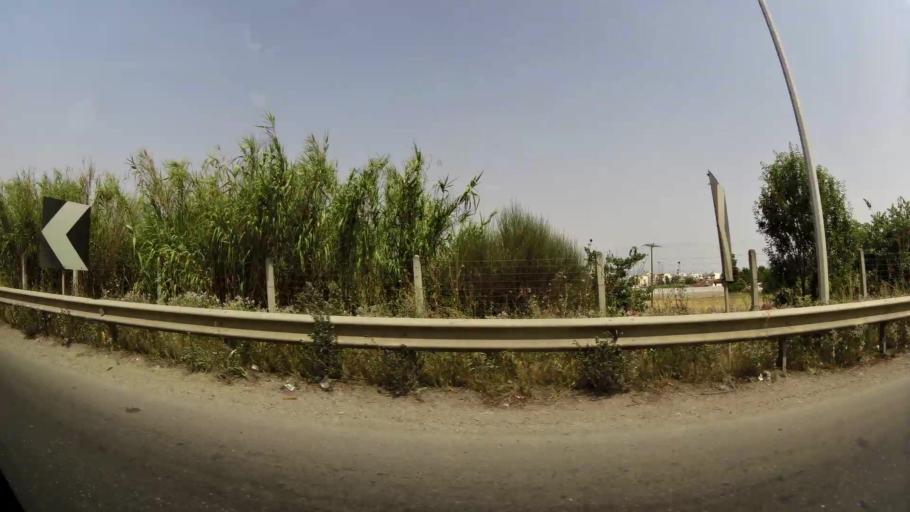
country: GR
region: Central Macedonia
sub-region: Nomos Thessalonikis
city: Nea Magnisia
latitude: 40.6936
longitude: 22.8484
